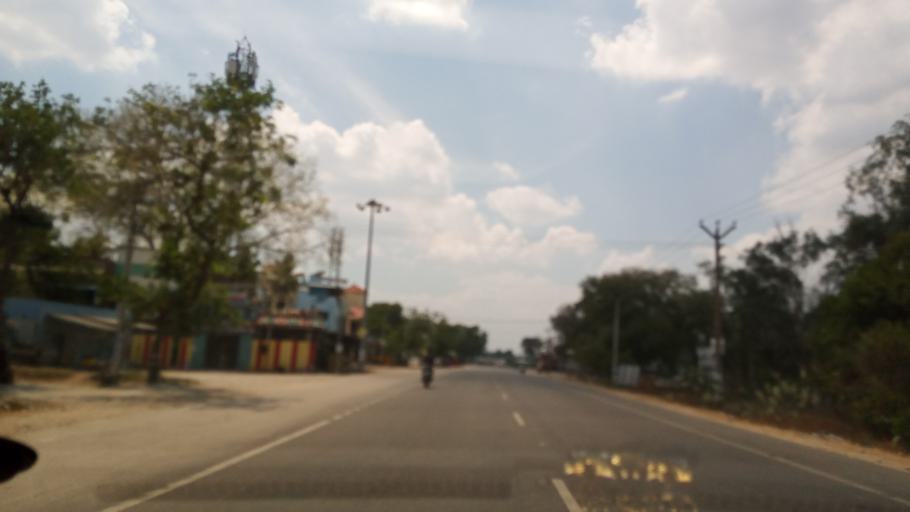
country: IN
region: Tamil Nadu
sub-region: Vellore
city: Walajapet
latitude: 12.9217
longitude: 79.3775
